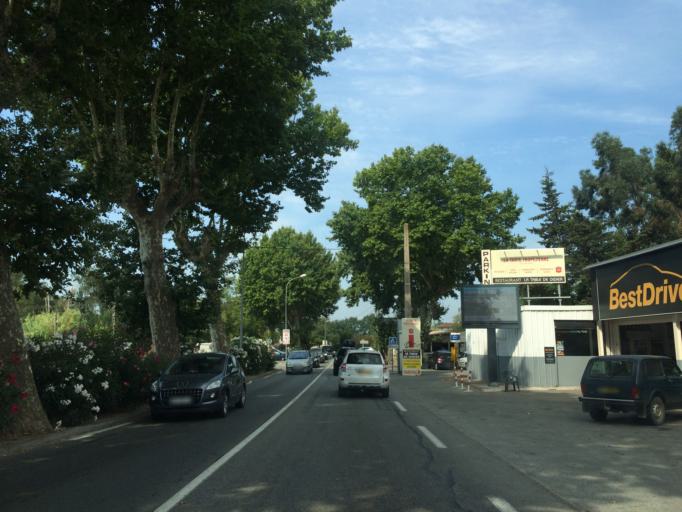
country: FR
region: Provence-Alpes-Cote d'Azur
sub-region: Departement du Var
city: Gassin
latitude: 43.2807
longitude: 6.5802
